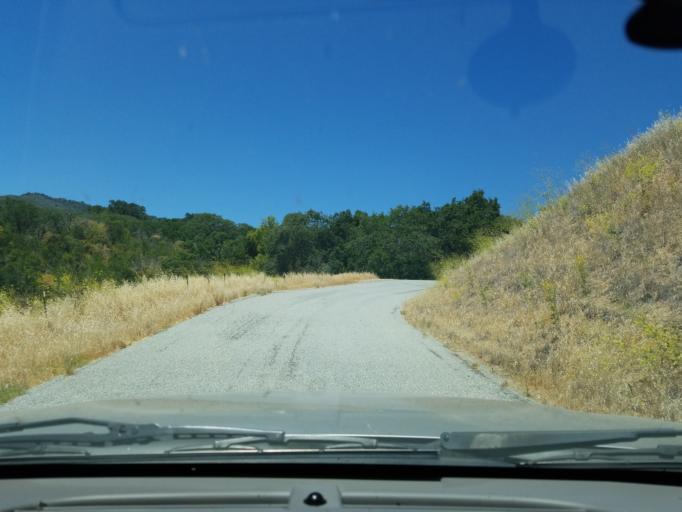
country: US
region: California
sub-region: Monterey County
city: Gonzales
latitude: 36.3411
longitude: -121.5161
